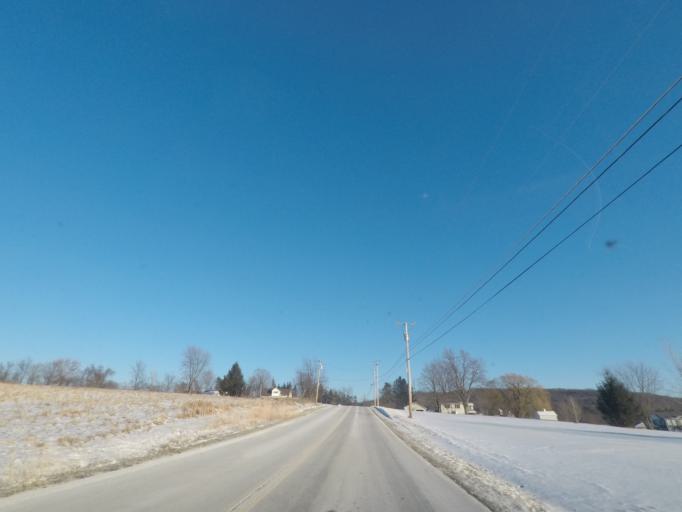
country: US
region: New York
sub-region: Saratoga County
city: Waterford
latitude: 42.8287
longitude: -73.6370
